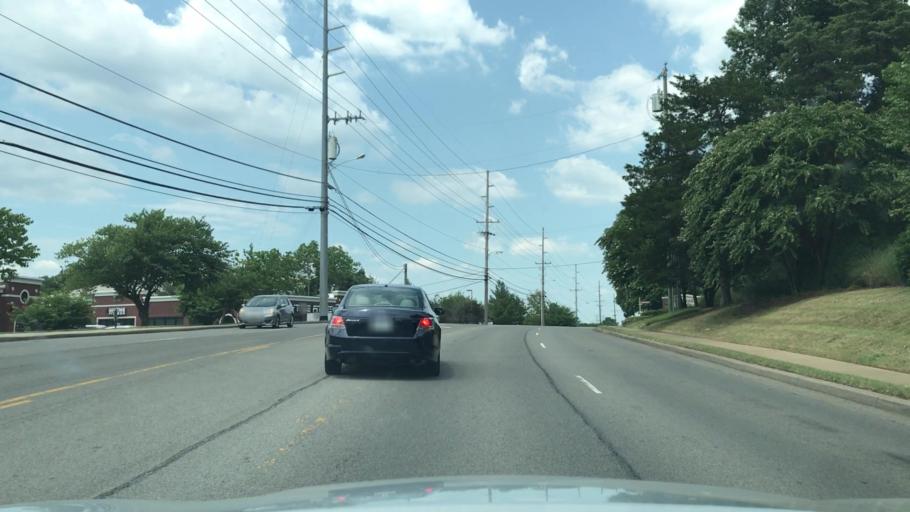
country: US
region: Tennessee
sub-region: Williamson County
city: Brentwood Estates
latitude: 36.0427
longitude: -86.7440
